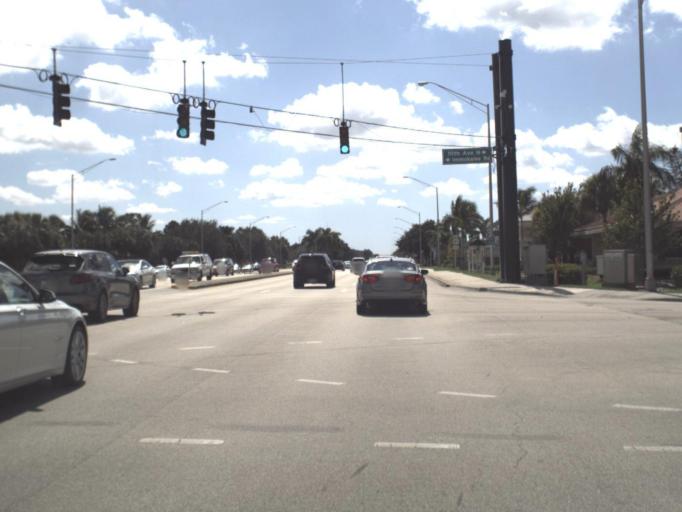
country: US
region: Florida
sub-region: Collier County
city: Naples Park
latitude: 26.2727
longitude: -81.8017
